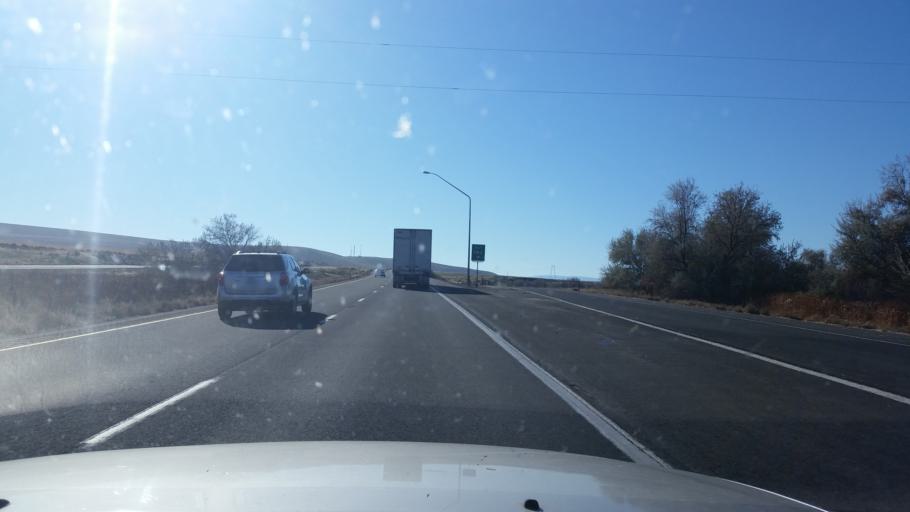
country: US
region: Washington
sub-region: Grant County
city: Quincy
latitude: 47.0250
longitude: -119.9414
